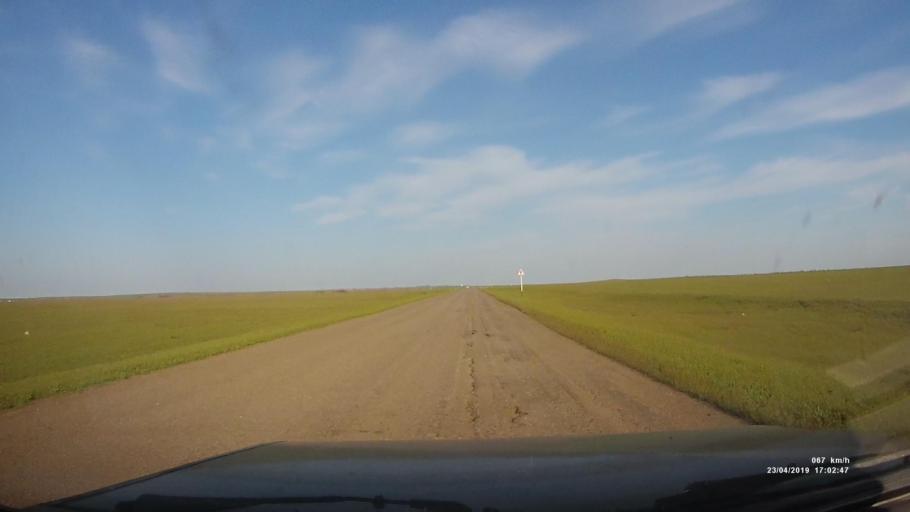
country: RU
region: Kalmykiya
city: Priyutnoye
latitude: 46.2915
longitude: 43.4224
